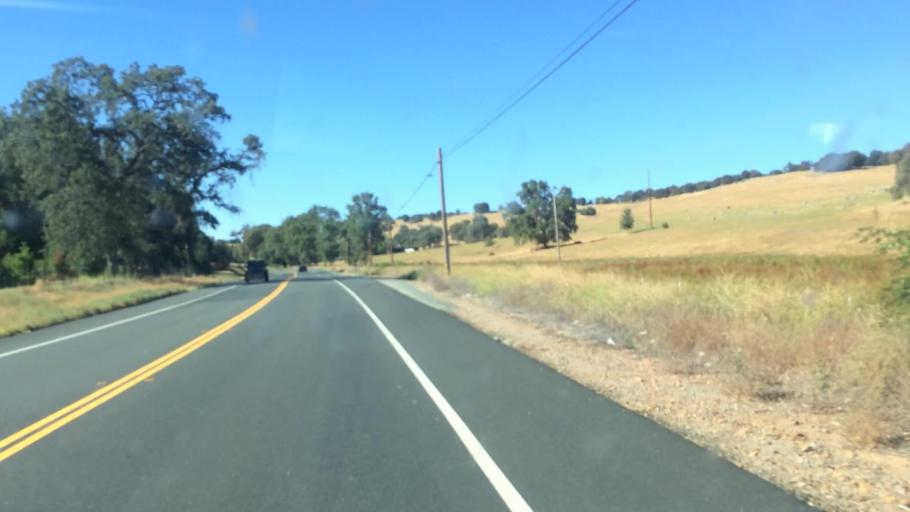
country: US
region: California
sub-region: El Dorado County
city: Deer Park
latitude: 38.6630
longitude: -120.8537
